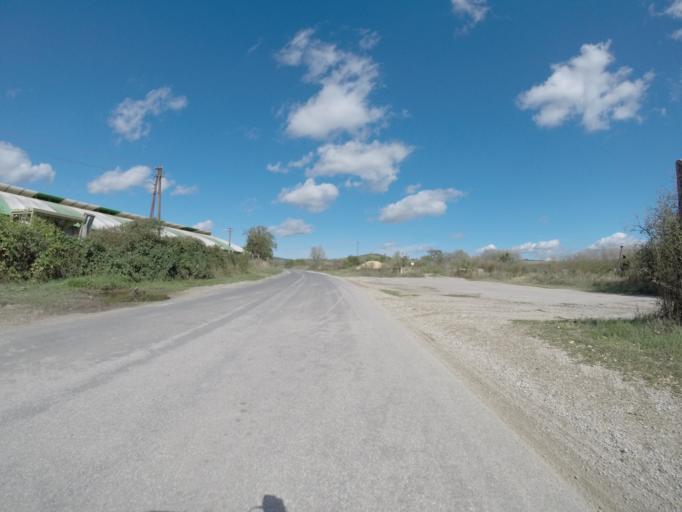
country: SK
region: Trenciansky
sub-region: Okres Nove Mesto nad Vahom
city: Nove Mesto nad Vahom
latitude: 48.7937
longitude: 17.7784
